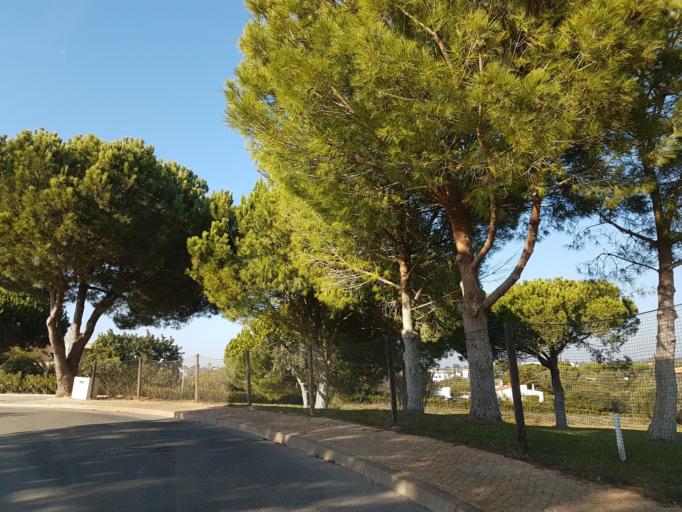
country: PT
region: Faro
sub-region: Albufeira
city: Albufeira
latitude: 37.0958
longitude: -8.2074
